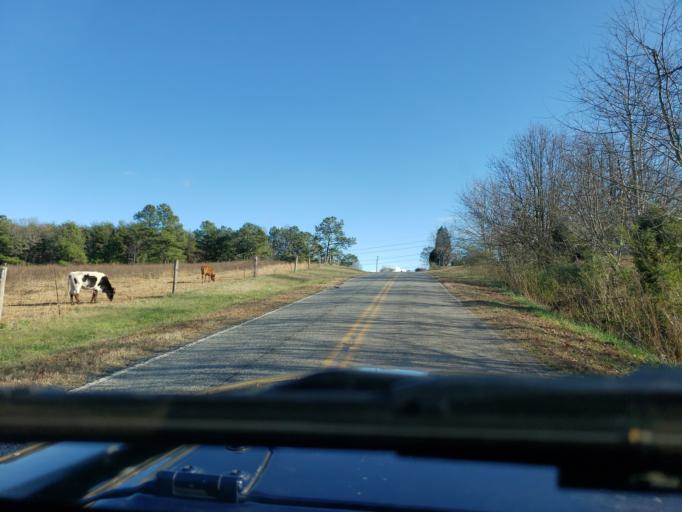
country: US
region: North Carolina
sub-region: Cleveland County
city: White Plains
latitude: 35.1647
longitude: -81.4246
